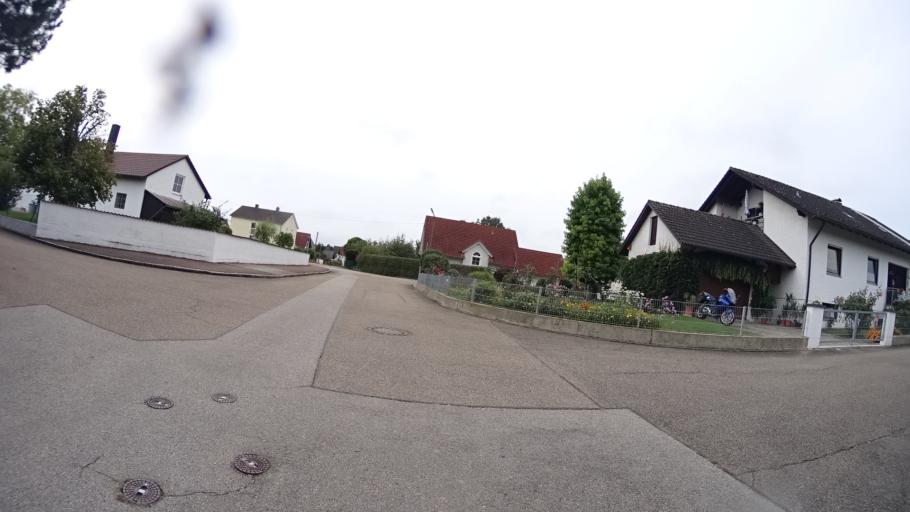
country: DE
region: Bavaria
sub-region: Upper Bavaria
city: Bohmfeld
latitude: 48.8374
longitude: 11.3558
